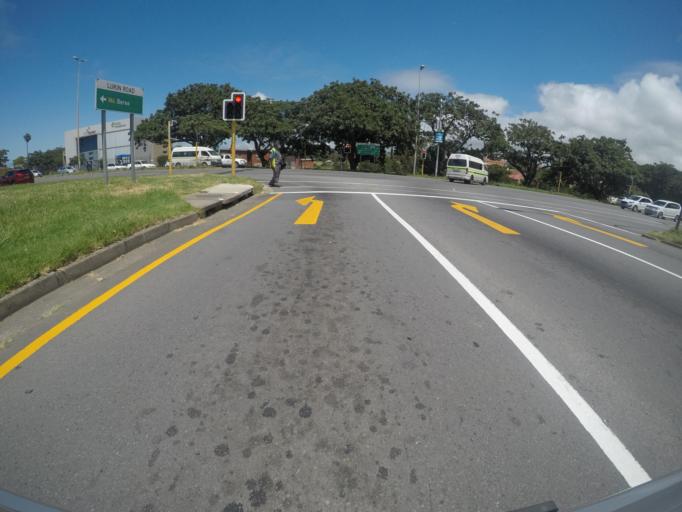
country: ZA
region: Eastern Cape
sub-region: Buffalo City Metropolitan Municipality
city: East London
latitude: -32.9965
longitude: 27.8976
